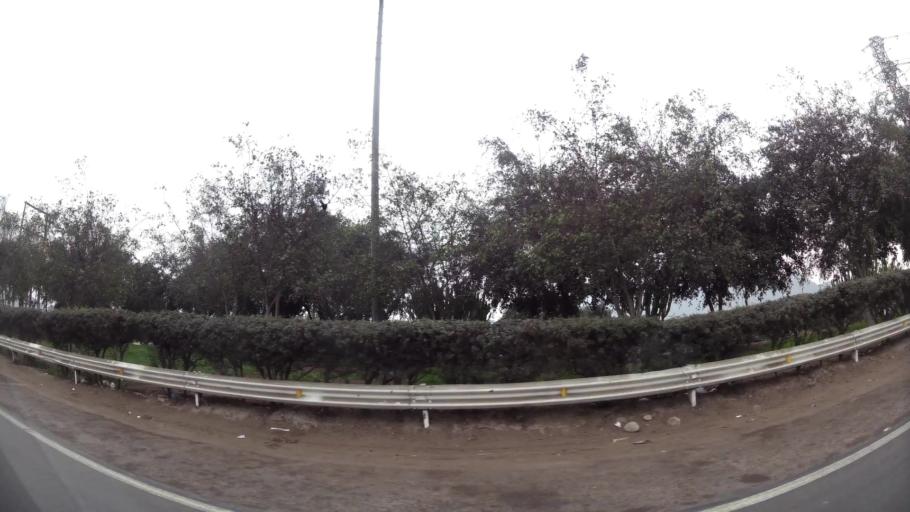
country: PE
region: Lima
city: Lima
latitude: -12.0324
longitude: -76.9901
